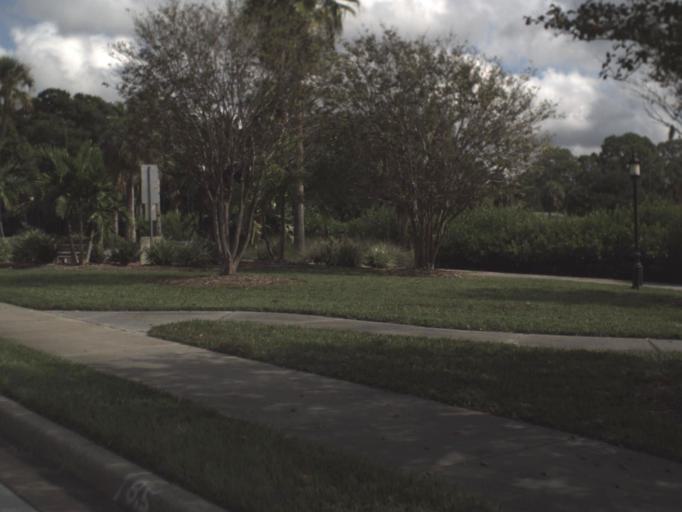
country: US
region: Florida
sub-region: Manatee County
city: Palmetto
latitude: 27.5114
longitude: -82.5728
